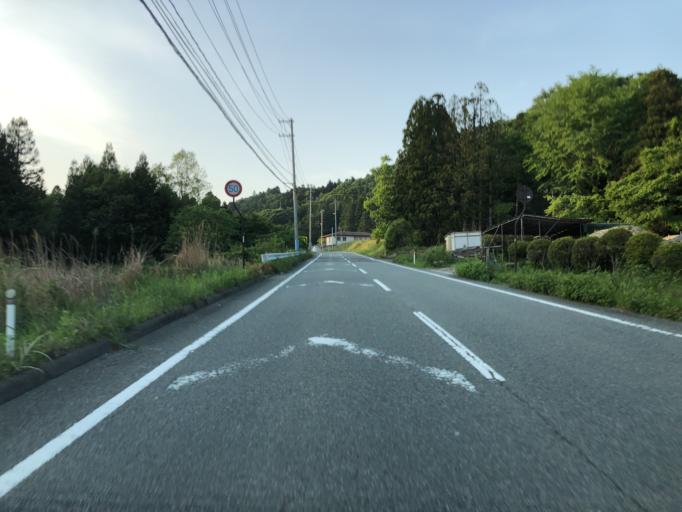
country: JP
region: Fukushima
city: Iwaki
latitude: 37.2373
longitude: 140.9775
